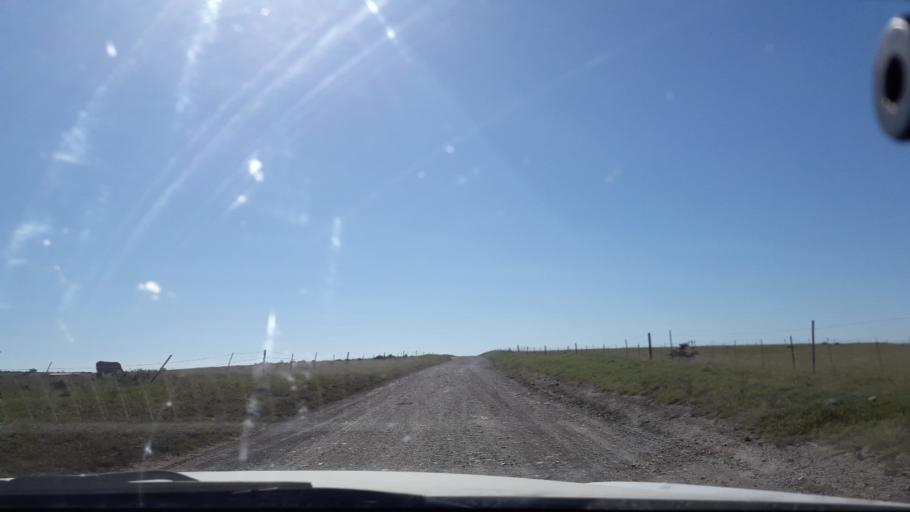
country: ZA
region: Eastern Cape
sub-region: Buffalo City Metropolitan Municipality
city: East London
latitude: -32.8010
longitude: 27.9501
